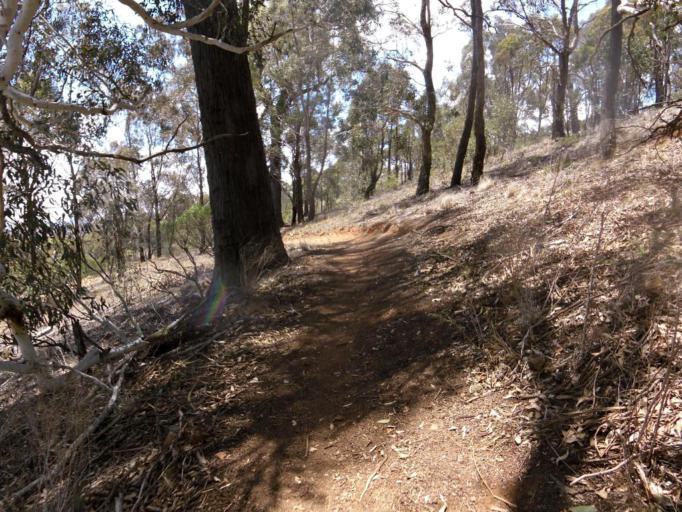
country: AU
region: Australian Capital Territory
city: Kaleen
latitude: -35.1402
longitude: 149.1477
